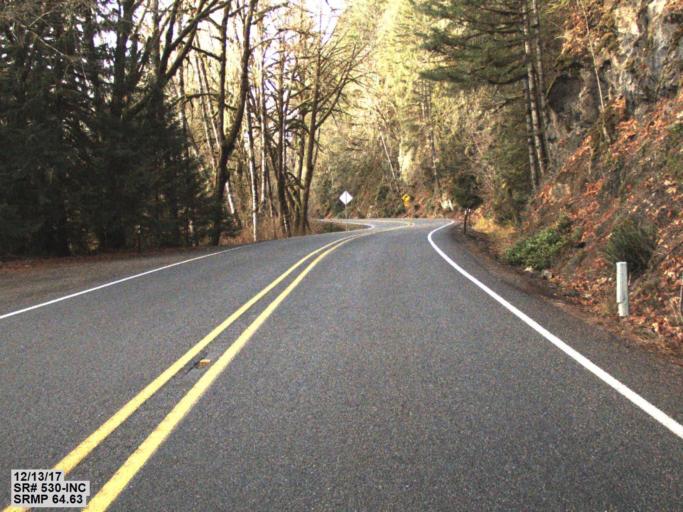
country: US
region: Washington
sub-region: Snohomish County
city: Darrington
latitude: 48.4487
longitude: -121.5868
